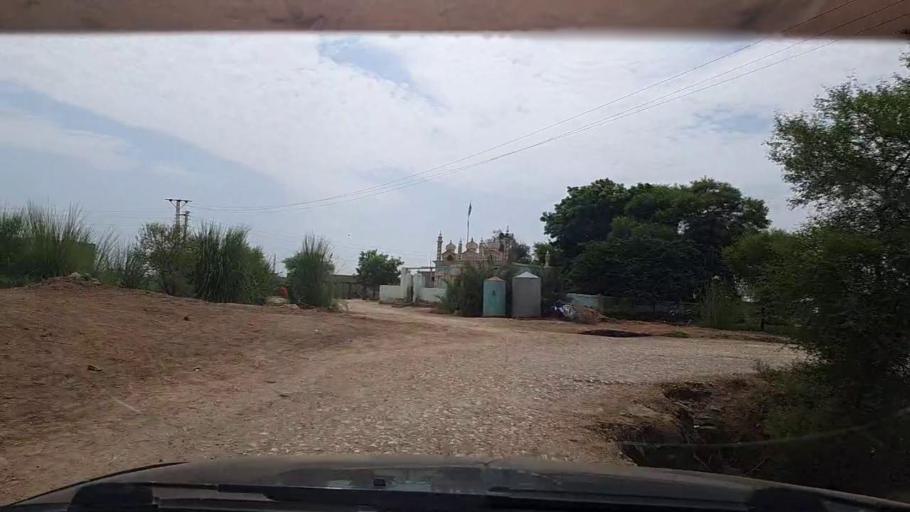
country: PK
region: Sindh
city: Thul
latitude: 28.2424
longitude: 68.7427
